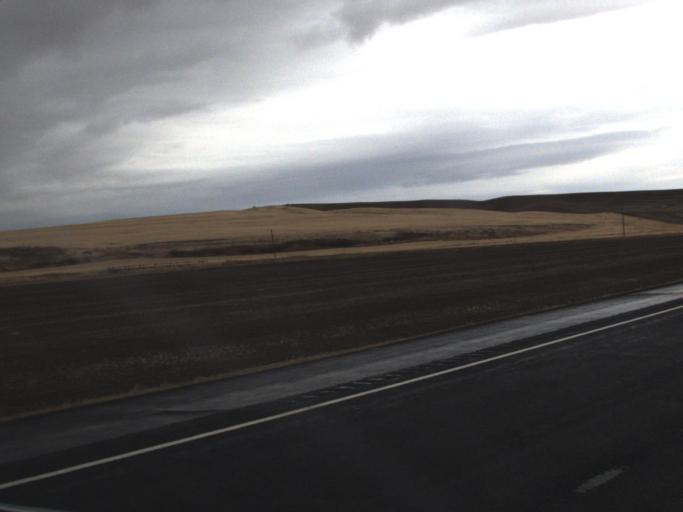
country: US
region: Washington
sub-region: Asotin County
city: Clarkston
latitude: 46.5608
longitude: -117.1078
